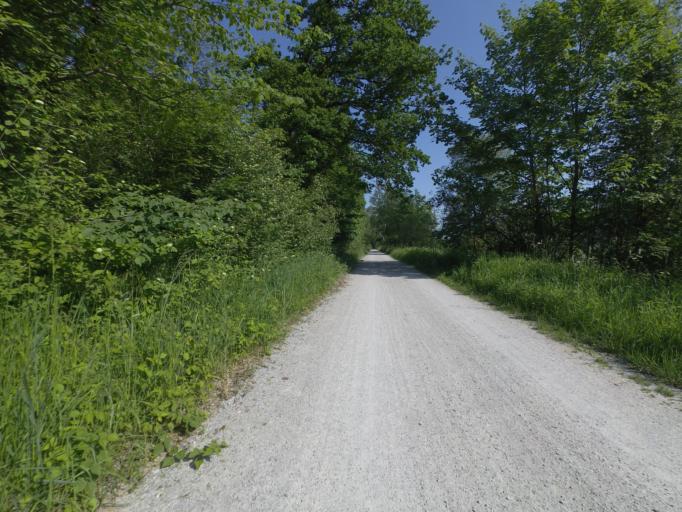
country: AT
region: Salzburg
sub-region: Politischer Bezirk Salzburg-Umgebung
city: Elsbethen
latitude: 47.7598
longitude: 13.0764
